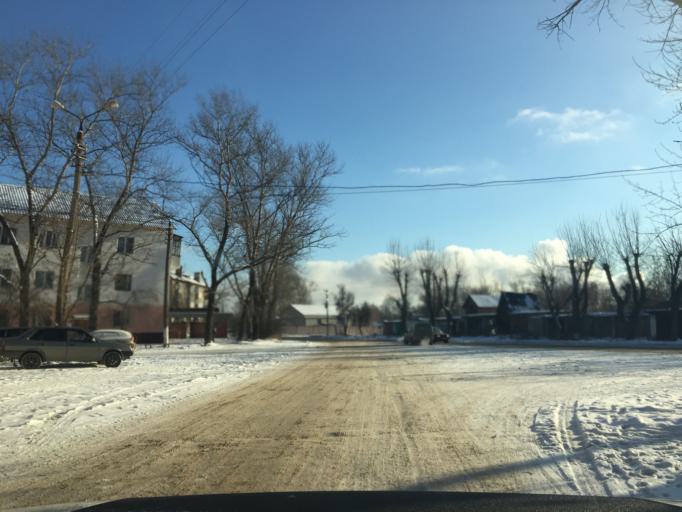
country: RU
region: Tula
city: Tula
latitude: 54.1786
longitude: 37.7039
